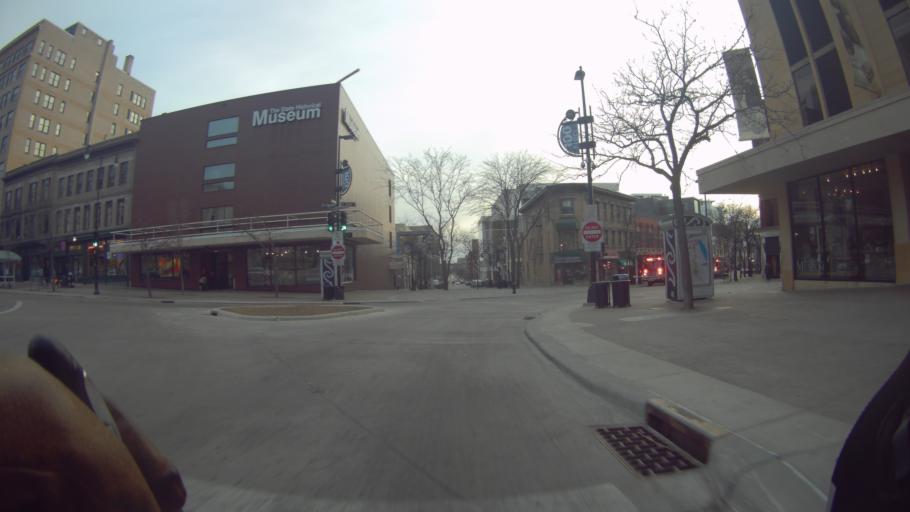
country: US
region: Wisconsin
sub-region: Dane County
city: Madison
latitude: 43.0748
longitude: -89.3862
